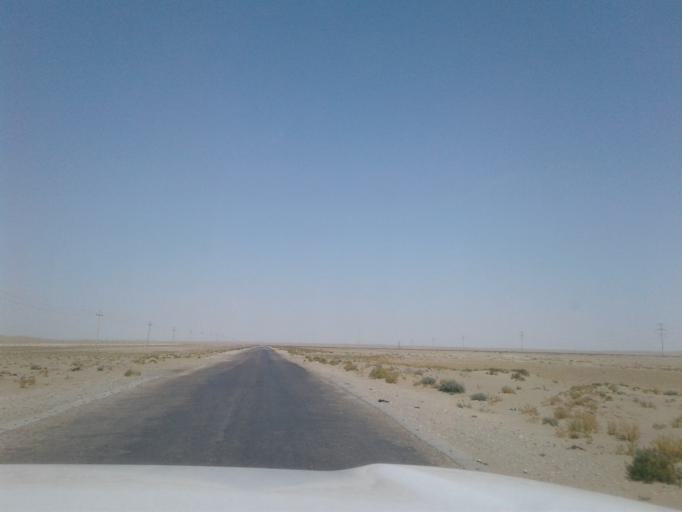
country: TM
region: Balkan
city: Gumdag
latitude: 38.3799
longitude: 54.3935
